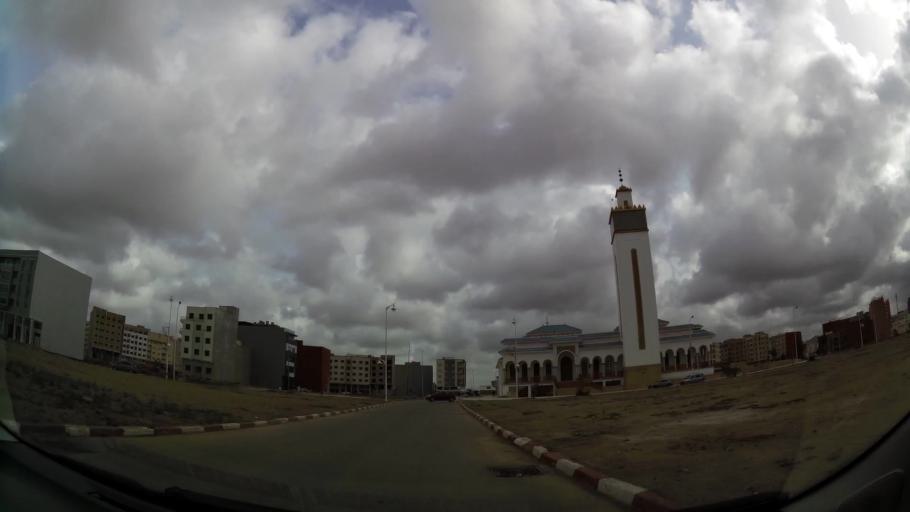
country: MA
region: Oriental
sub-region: Nador
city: Nador
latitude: 35.1530
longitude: -2.9189
